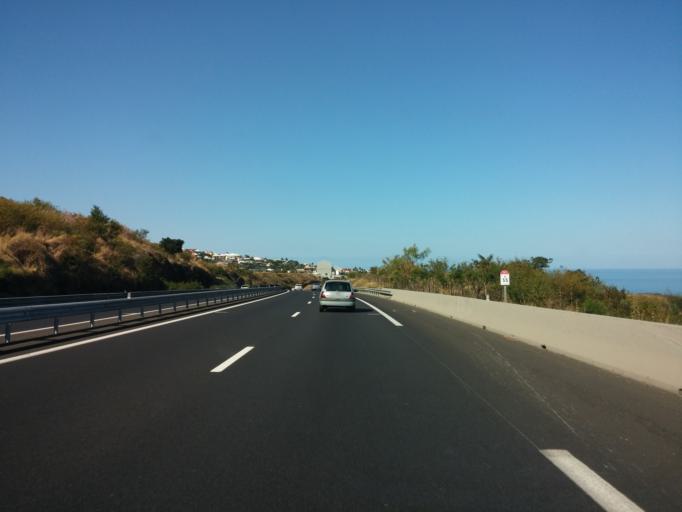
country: RE
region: Reunion
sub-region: Reunion
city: Saint-Leu
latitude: -21.1922
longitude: 55.2962
